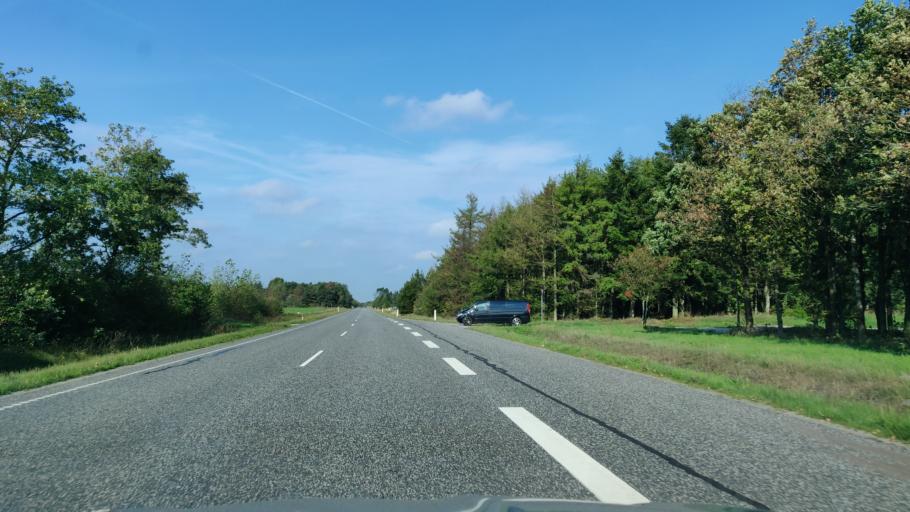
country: DK
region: Central Jutland
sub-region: Herning Kommune
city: Sunds
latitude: 56.2440
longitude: 9.0814
